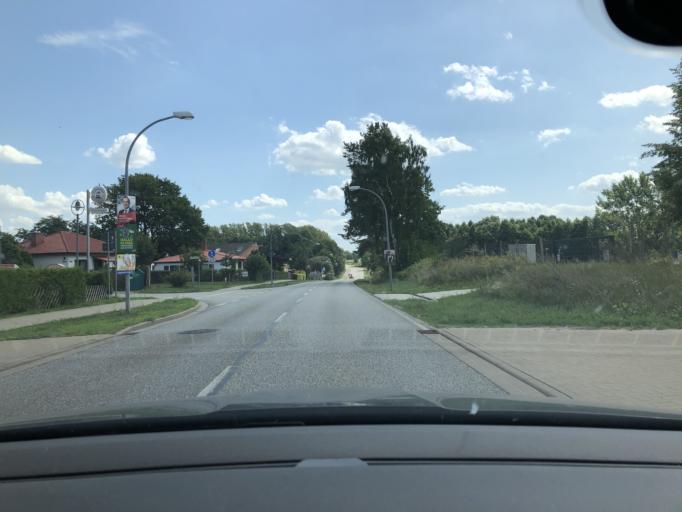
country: DE
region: Brandenburg
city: Neuruppin
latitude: 52.9445
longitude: 12.8512
